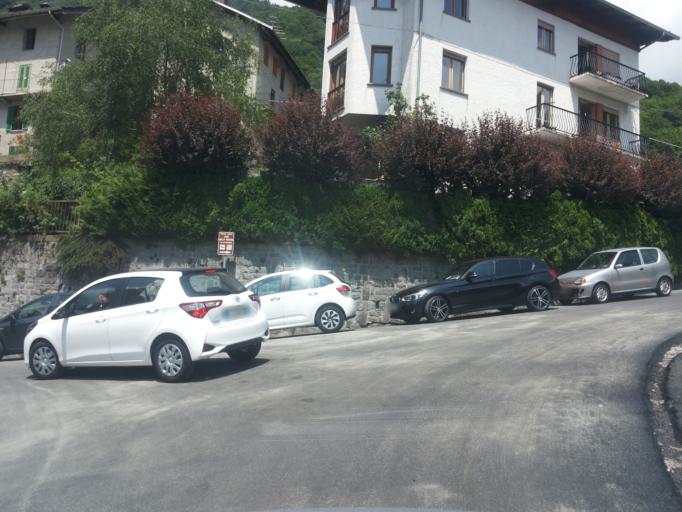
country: IT
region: Piedmont
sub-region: Provincia di Biella
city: Piedicavallo
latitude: 45.6889
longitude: 7.9529
